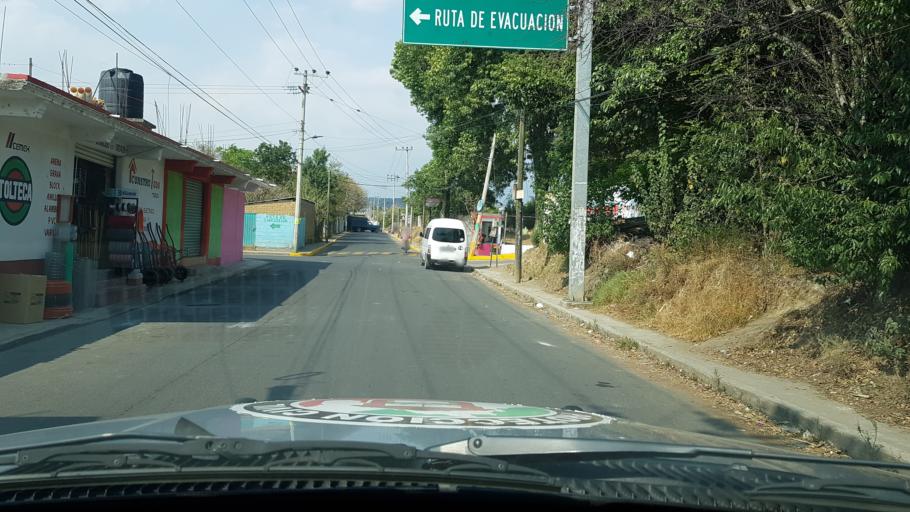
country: MX
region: Mexico
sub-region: Ozumba
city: San Jose Tlacotitlan
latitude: 18.9832
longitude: -98.8086
